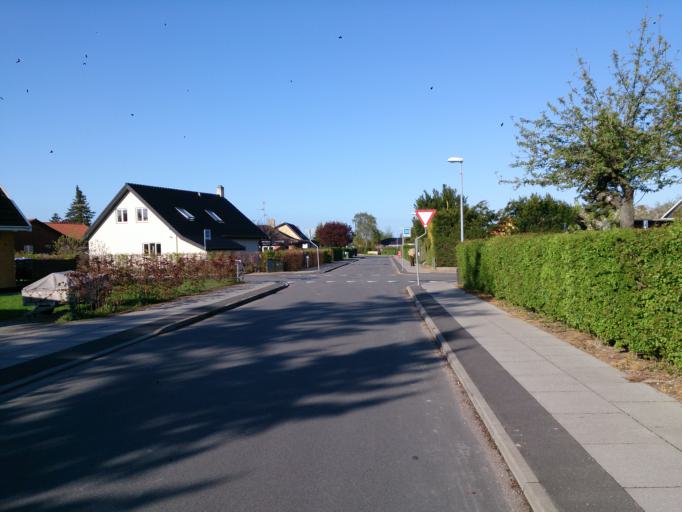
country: DK
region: Capital Region
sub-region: Tarnby Kommune
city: Tarnby
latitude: 55.6185
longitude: 12.5827
